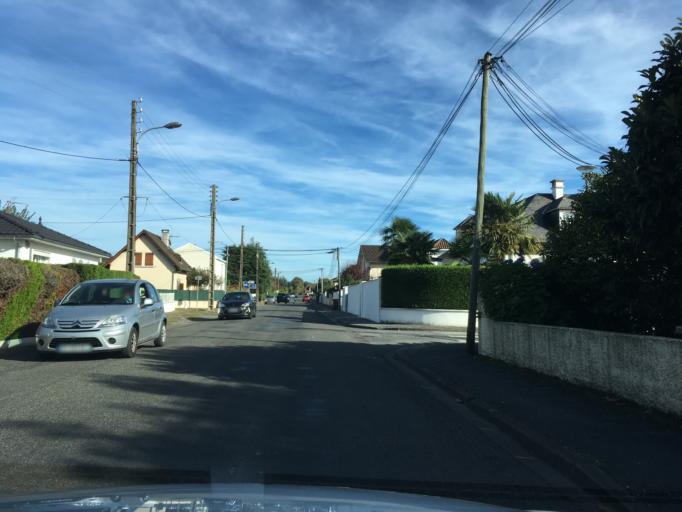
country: FR
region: Aquitaine
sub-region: Departement des Pyrenees-Atlantiques
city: Pau
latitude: 43.3289
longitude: -0.3714
